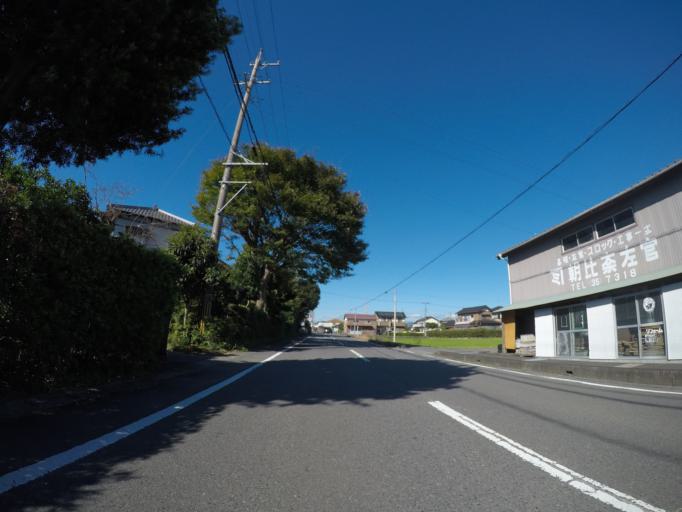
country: JP
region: Shizuoka
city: Fujieda
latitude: 34.8290
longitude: 138.2399
